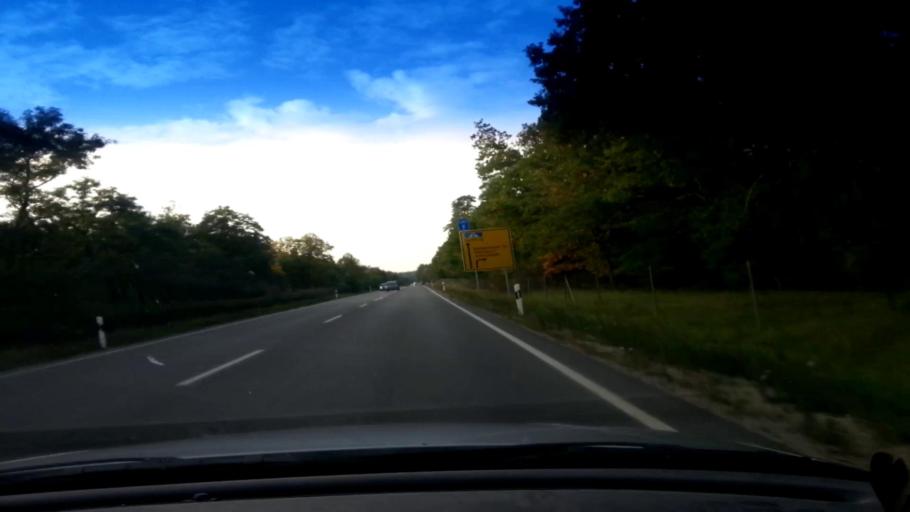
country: DE
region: Bavaria
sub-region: Upper Franconia
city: Strullendorf
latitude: 49.8558
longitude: 10.9558
